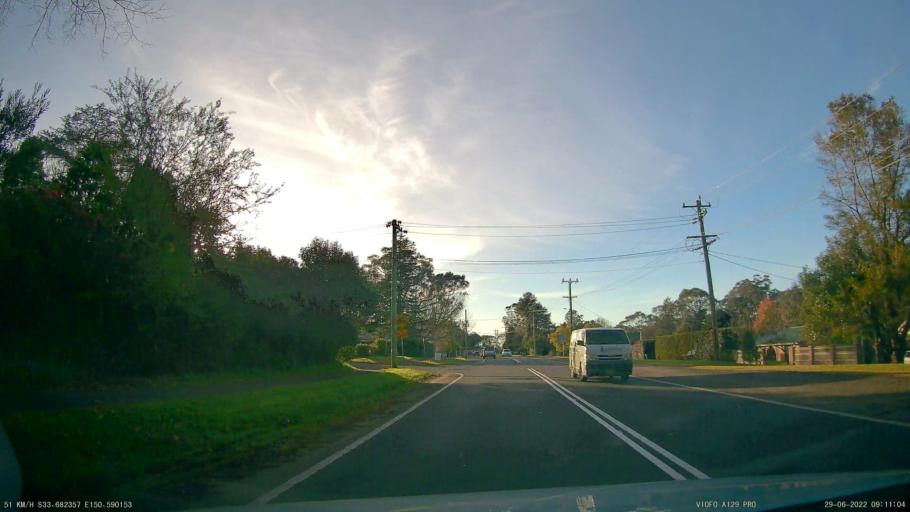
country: AU
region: New South Wales
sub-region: Blue Mountains Municipality
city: Blaxland
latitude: -33.6823
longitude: 150.5906
